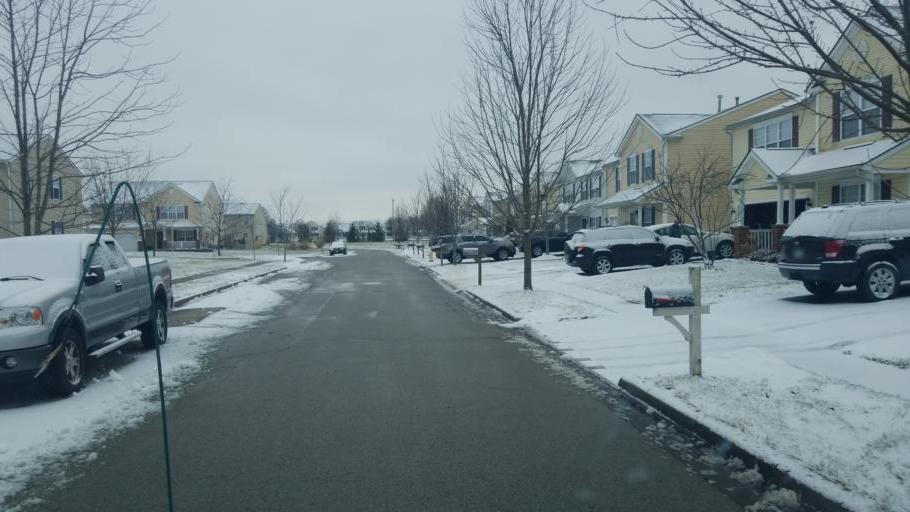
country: US
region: Ohio
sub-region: Franklin County
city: Reynoldsburg
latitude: 40.0121
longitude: -82.7929
